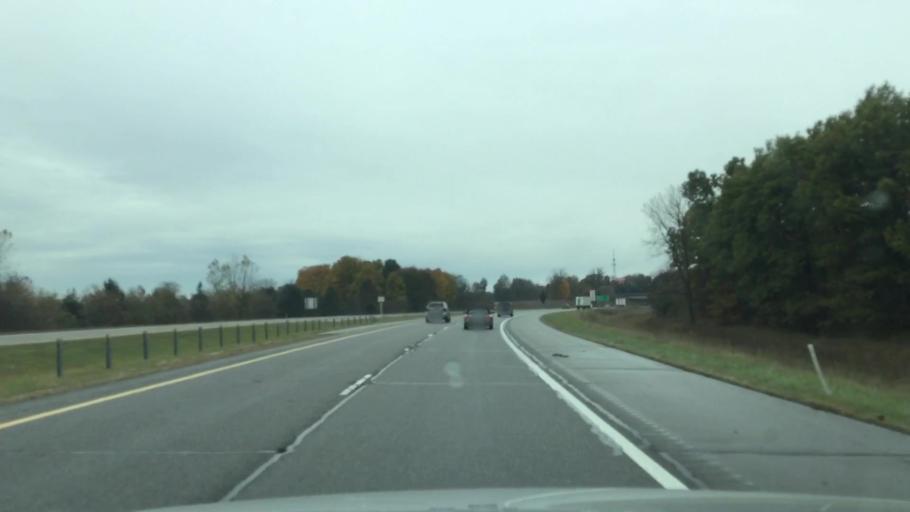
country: US
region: Michigan
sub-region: Calhoun County
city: Albion
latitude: 42.2650
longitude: -84.7695
